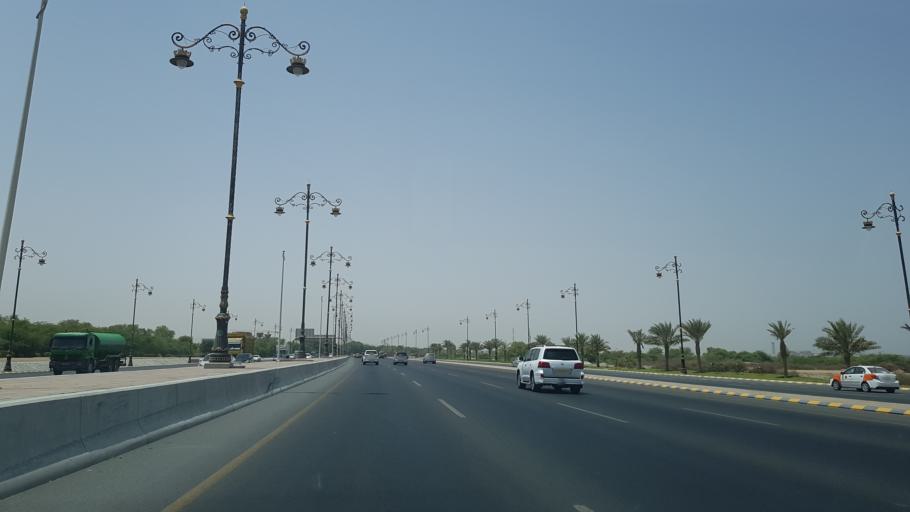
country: OM
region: Muhafazat Masqat
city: Bawshar
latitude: 23.5920
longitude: 58.3256
